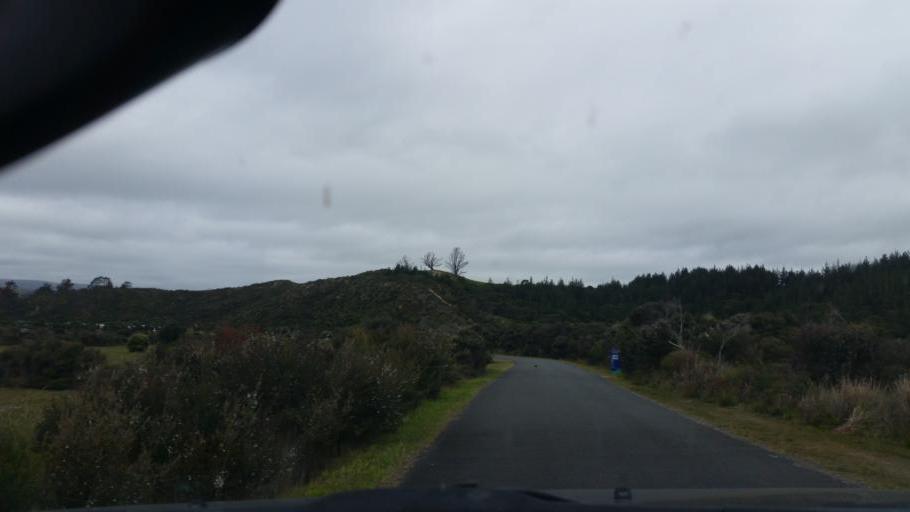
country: NZ
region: Northland
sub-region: Kaipara District
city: Dargaville
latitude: -35.8121
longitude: 173.6577
